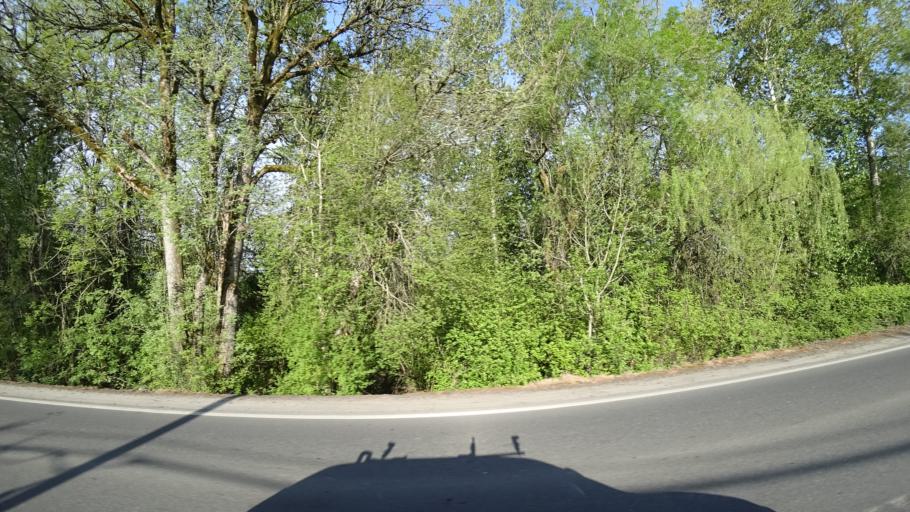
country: US
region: Oregon
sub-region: Washington County
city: Hillsboro
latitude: 45.5117
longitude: -122.9910
